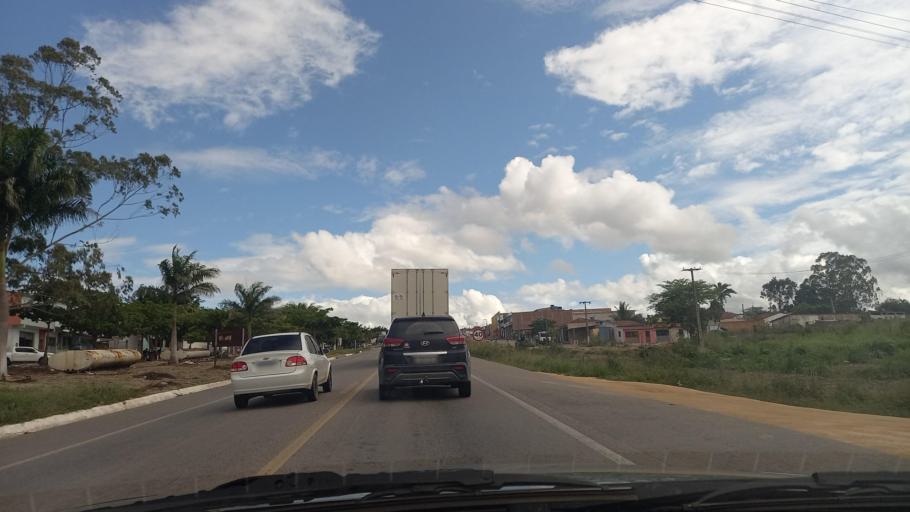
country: BR
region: Pernambuco
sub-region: Lajedo
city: Lajedo
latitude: -8.7074
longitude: -36.4182
